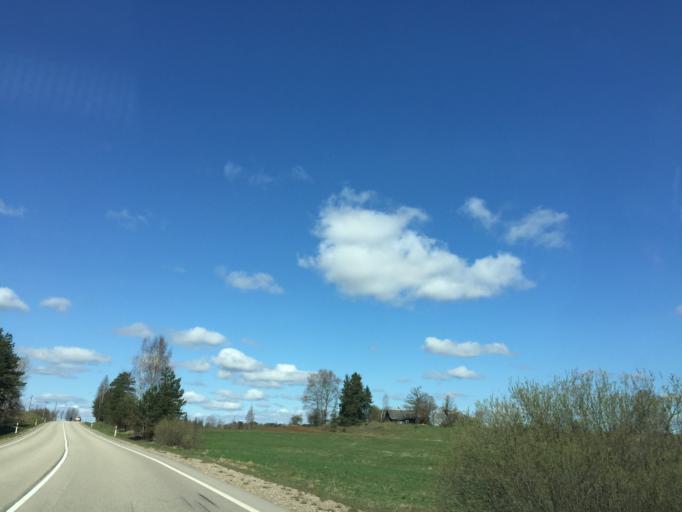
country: LV
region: Rezekne
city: Rezekne
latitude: 56.5713
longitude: 27.2710
